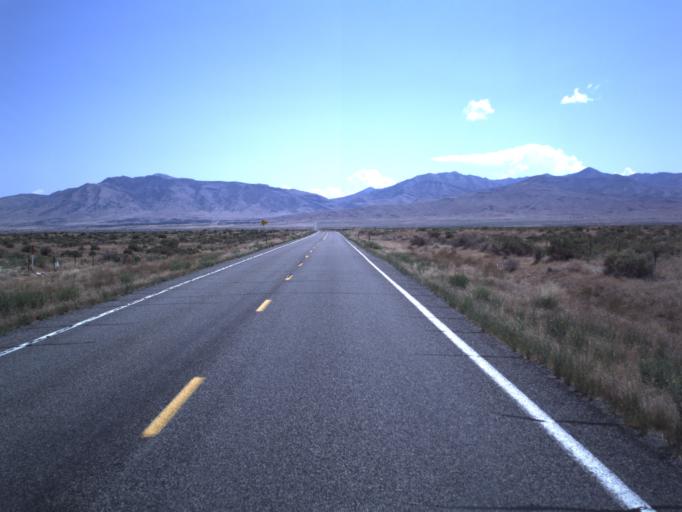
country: US
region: Utah
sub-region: Millard County
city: Delta
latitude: 39.3534
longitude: -112.4740
